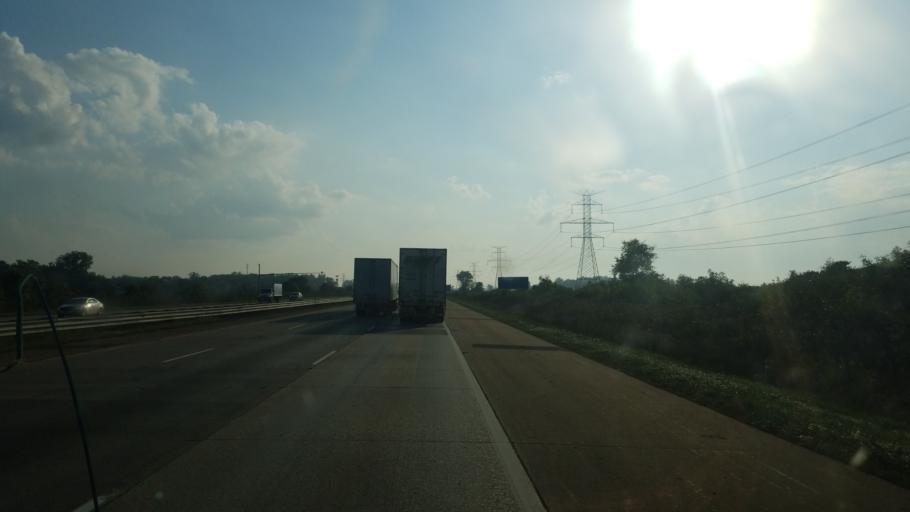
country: US
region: Michigan
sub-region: Monroe County
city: Luna Pier
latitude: 41.8209
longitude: -83.4391
